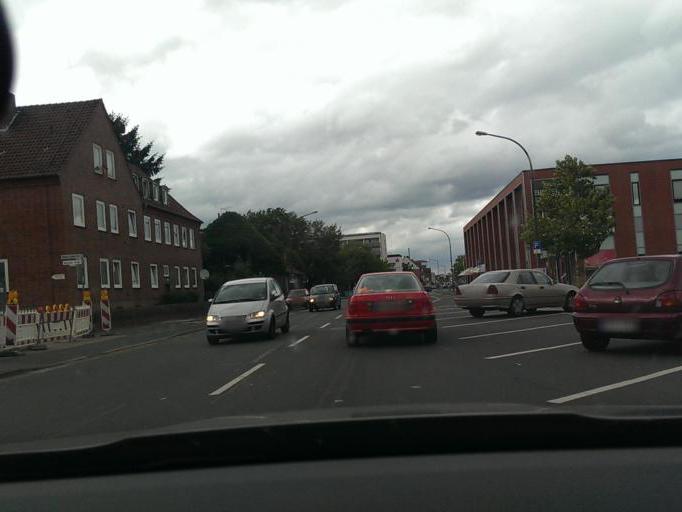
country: DE
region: Lower Saxony
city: Langenhagen
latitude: 52.4461
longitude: 9.7387
